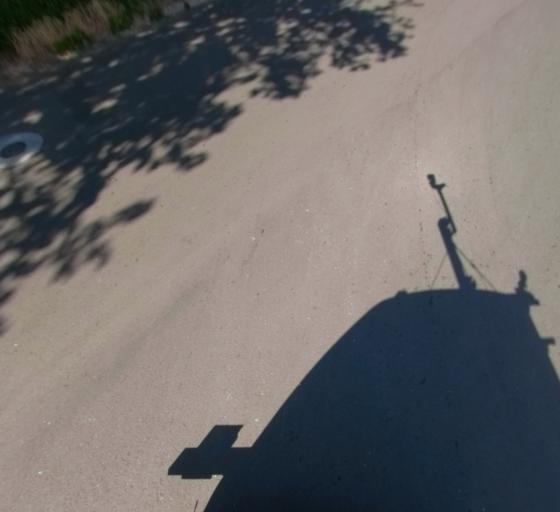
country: US
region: California
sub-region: Madera County
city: Parkwood
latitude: 36.9365
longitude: -120.0546
